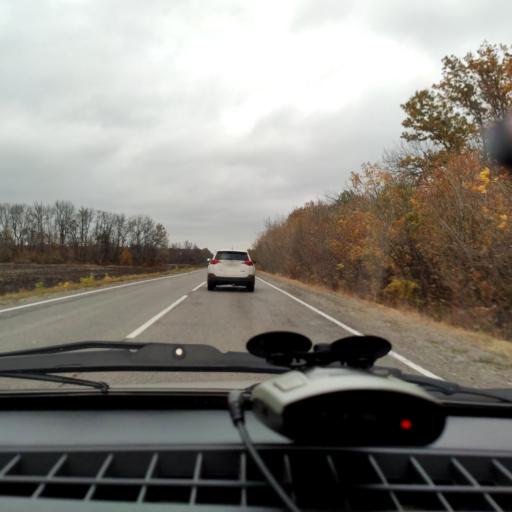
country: RU
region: Voronezj
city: Shilovo
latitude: 51.4143
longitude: 39.0055
